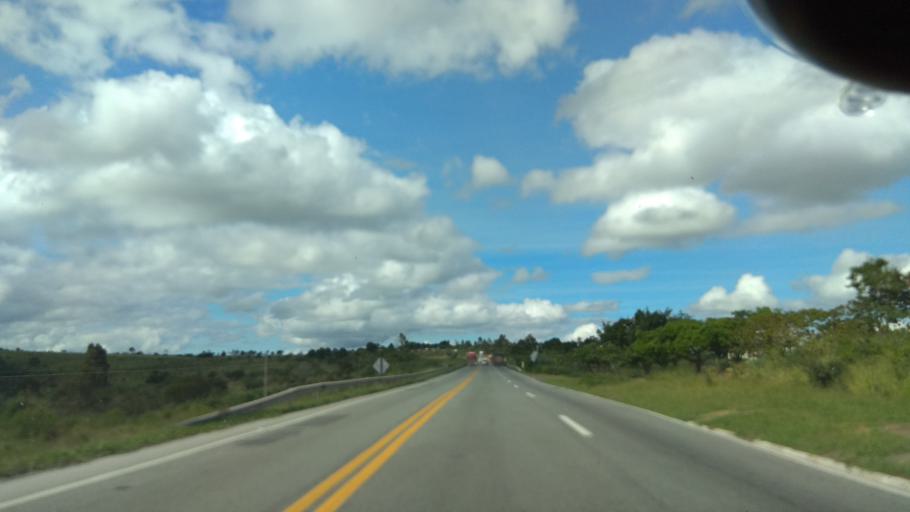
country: BR
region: Bahia
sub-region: Santa Ines
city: Santa Ines
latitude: -13.1079
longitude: -39.9751
